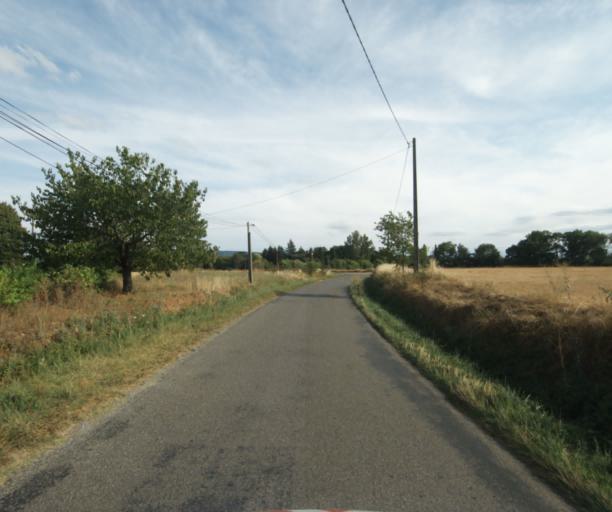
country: FR
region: Midi-Pyrenees
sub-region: Departement de la Haute-Garonne
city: Revel
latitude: 43.4776
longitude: 1.9906
